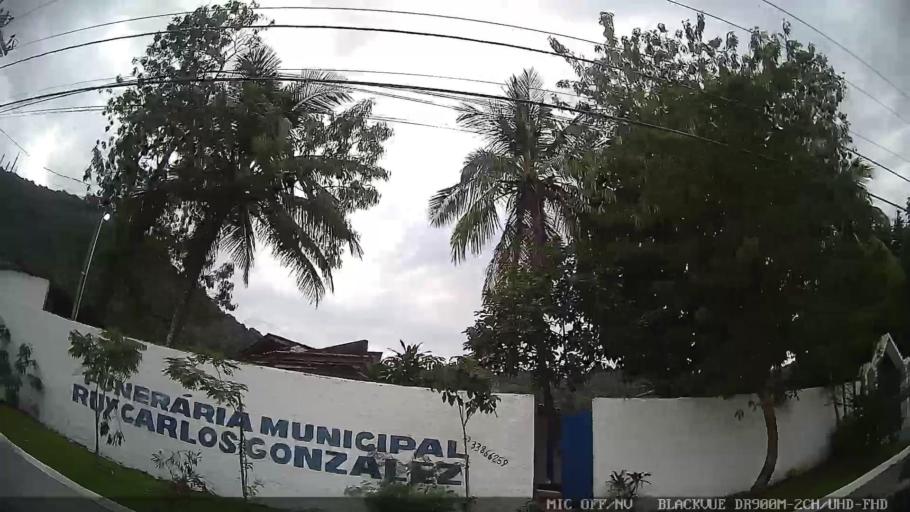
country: BR
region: Sao Paulo
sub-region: Guaruja
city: Guaruja
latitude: -23.9839
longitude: -46.2473
